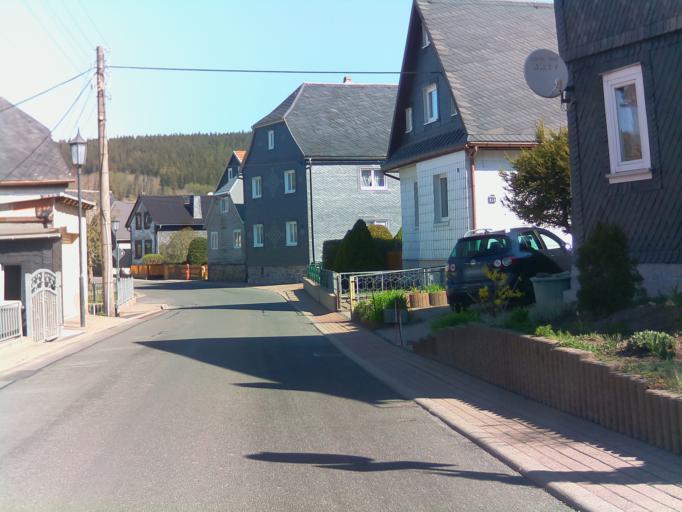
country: DE
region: Thuringia
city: Gillersdorf
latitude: 50.6035
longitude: 11.0205
